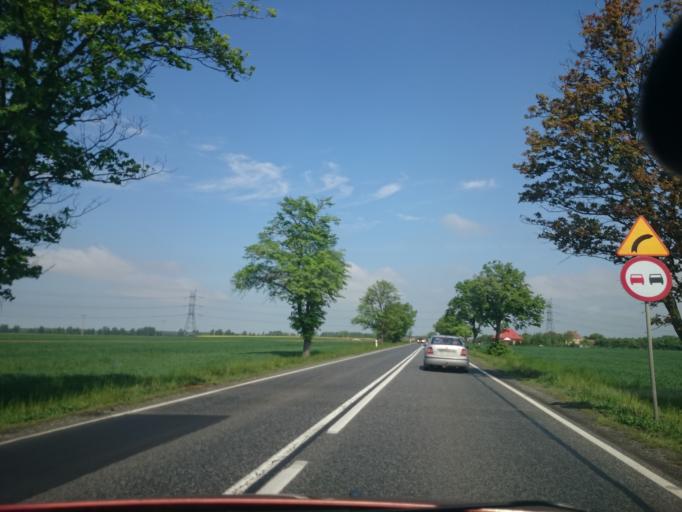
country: PL
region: Opole Voivodeship
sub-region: Powiat opolski
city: Dabrowa
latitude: 50.7118
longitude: 17.7755
